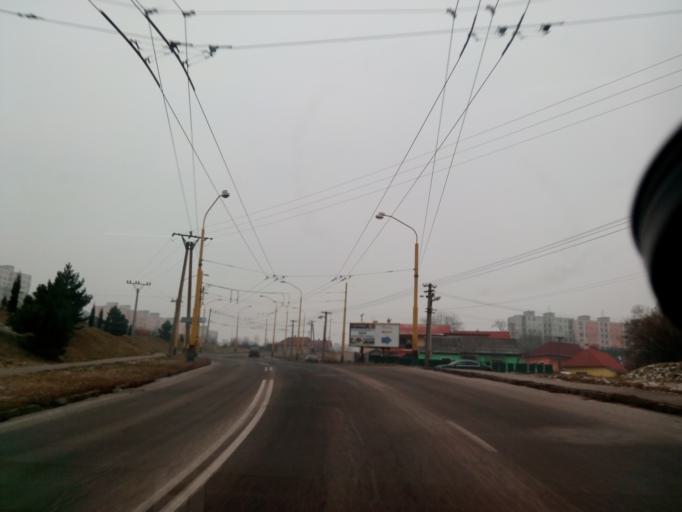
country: SK
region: Kosicky
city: Kosice
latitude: 48.7098
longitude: 21.2060
